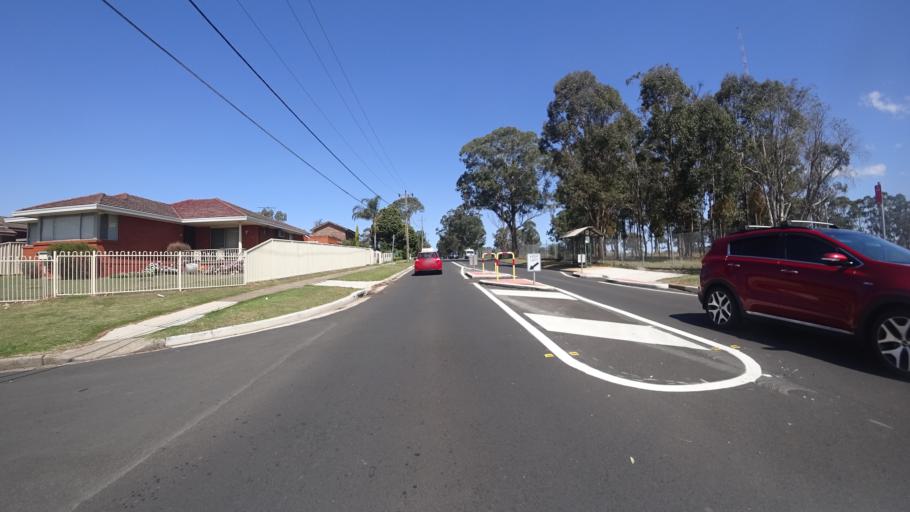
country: AU
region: New South Wales
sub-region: Liverpool
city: Miller
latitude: -33.9400
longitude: 150.8892
